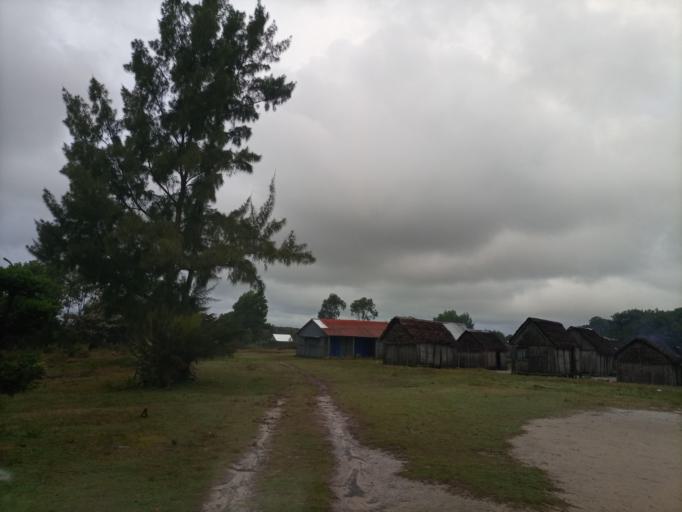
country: MG
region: Anosy
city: Fort Dauphin
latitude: -24.6480
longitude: 47.2093
